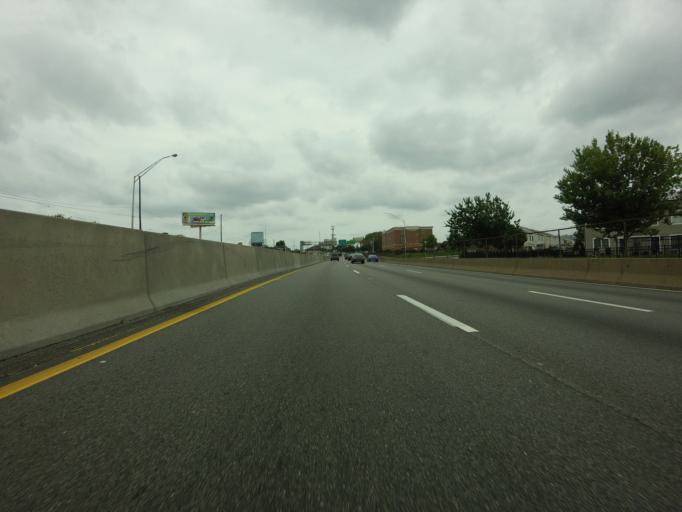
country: US
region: Pennsylvania
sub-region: Philadelphia County
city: Philadelphia
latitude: 39.9297
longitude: -75.1979
